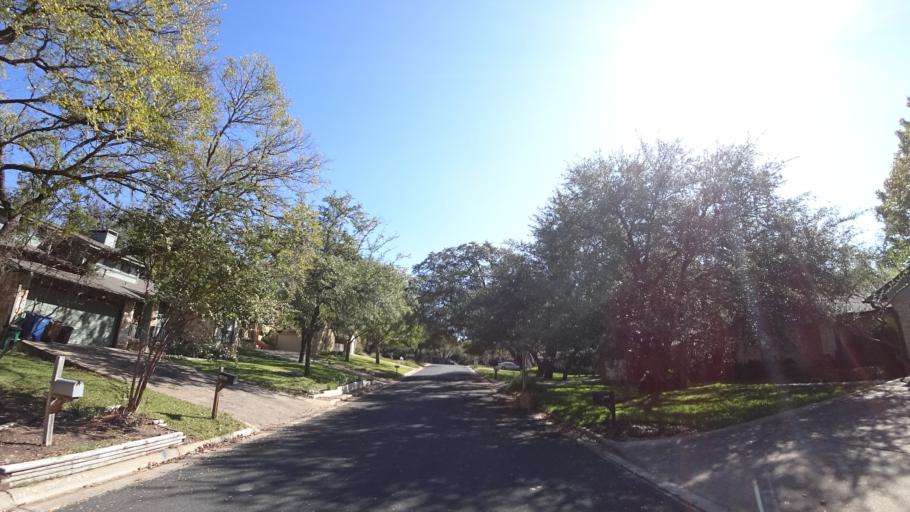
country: US
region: Texas
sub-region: Williamson County
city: Jollyville
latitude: 30.4238
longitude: -97.7673
